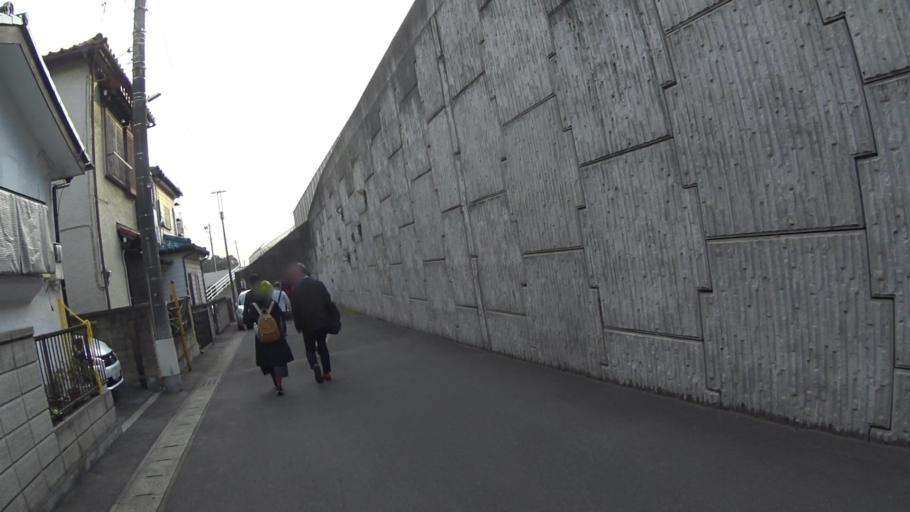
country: JP
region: Chiba
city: Funabashi
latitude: 35.6876
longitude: 140.0034
